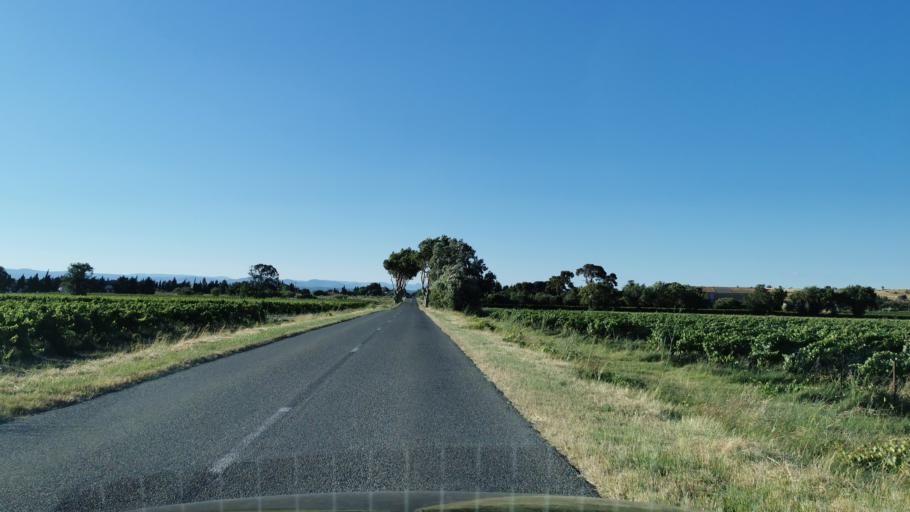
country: FR
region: Languedoc-Roussillon
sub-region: Departement de l'Aude
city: Ouveillan
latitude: 43.2598
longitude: 2.9959
